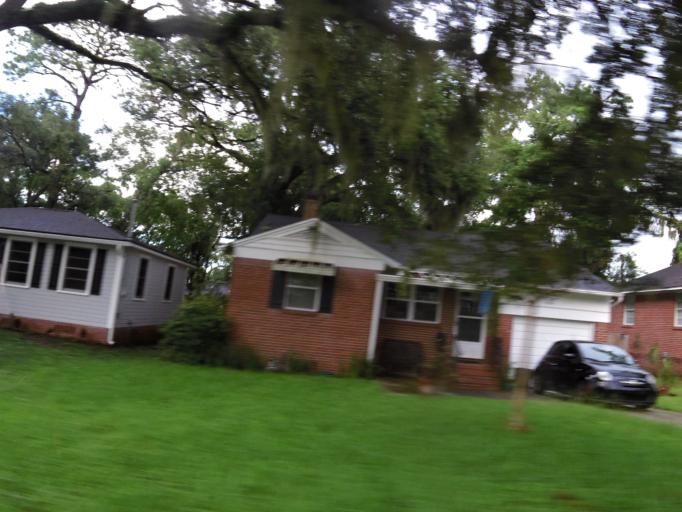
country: US
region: Florida
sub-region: Duval County
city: Jacksonville
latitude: 30.3067
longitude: -81.6307
